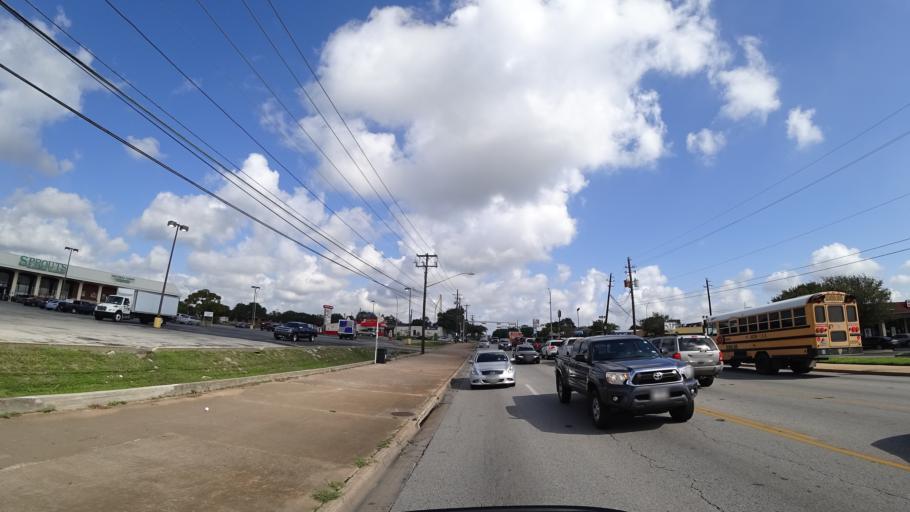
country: US
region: Texas
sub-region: Travis County
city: Shady Hollow
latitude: 30.2019
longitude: -97.8071
